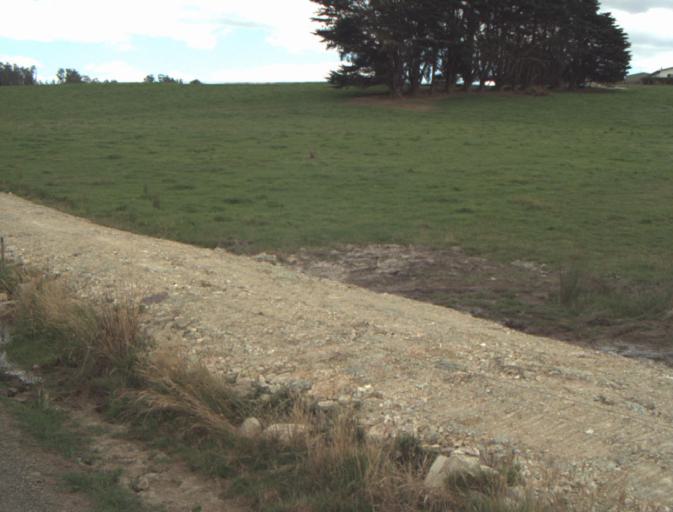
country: AU
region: Tasmania
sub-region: Launceston
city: Mayfield
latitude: -41.2376
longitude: 147.2068
